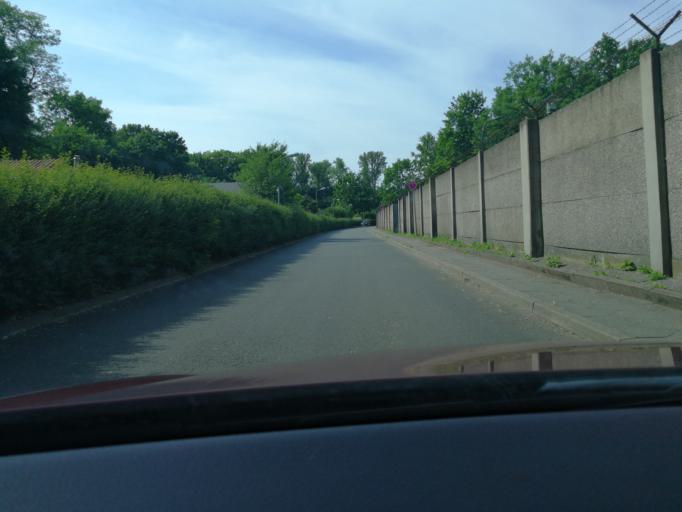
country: DE
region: Berlin
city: Reinickendorf
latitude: 52.5515
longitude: 13.3236
